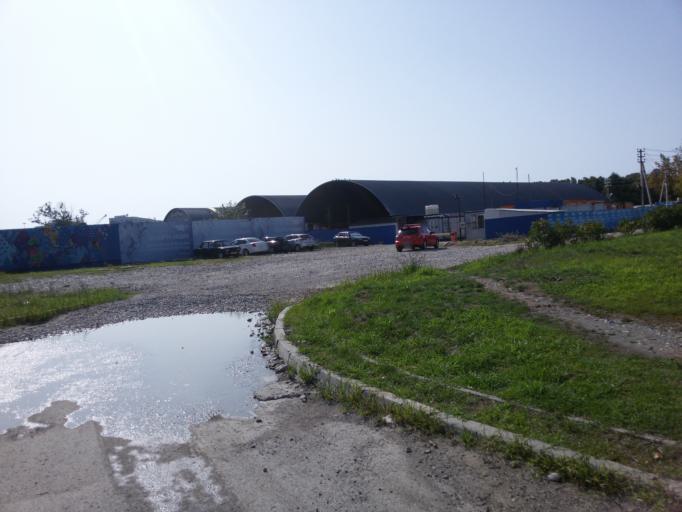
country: RU
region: Krasnodarskiy
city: Adler
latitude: 43.4161
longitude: 39.9392
